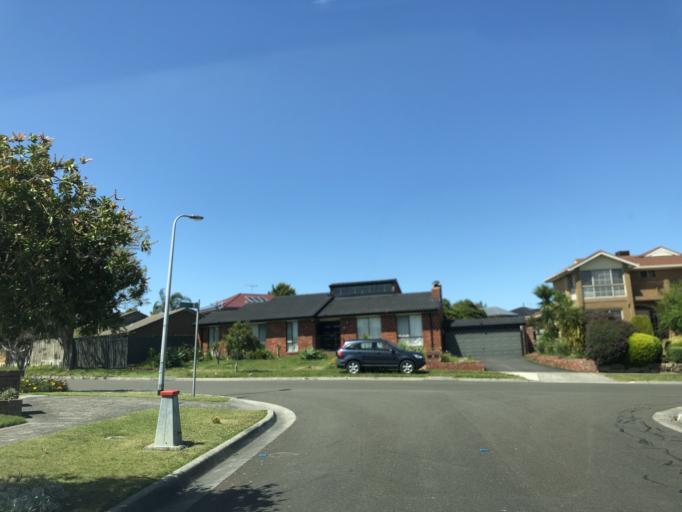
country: AU
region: Victoria
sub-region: Casey
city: Endeavour Hills
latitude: -37.9717
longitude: 145.2719
